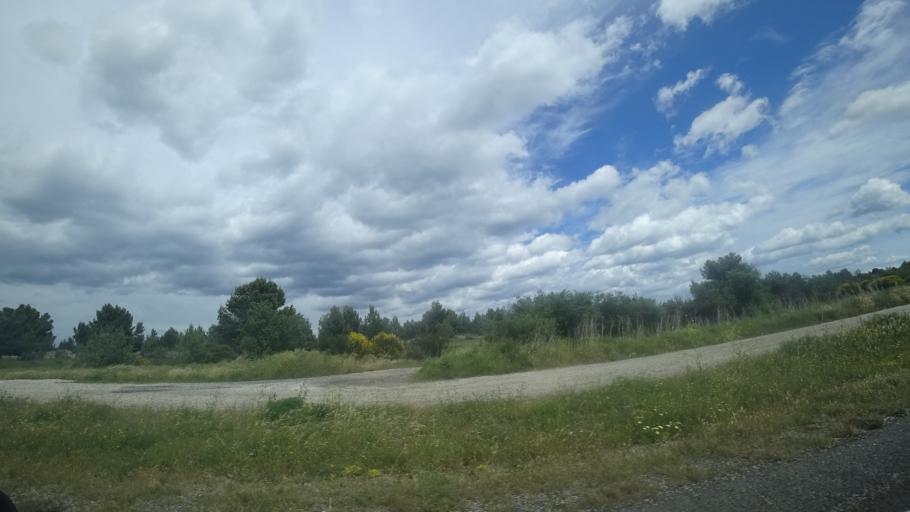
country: FR
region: Languedoc-Roussillon
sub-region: Departement de l'Aude
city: Leucate
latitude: 42.9249
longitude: 3.0186
